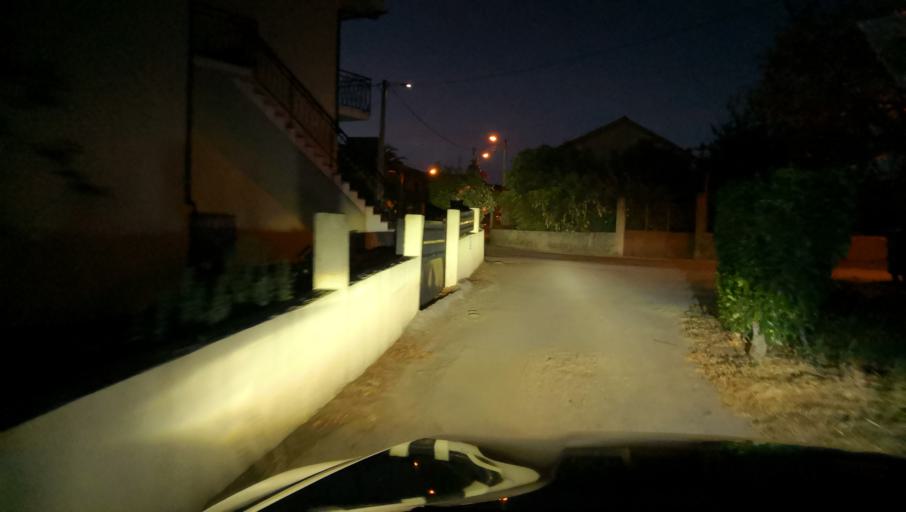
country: PT
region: Vila Real
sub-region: Sabrosa
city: Vilela
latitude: 41.2590
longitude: -7.6534
